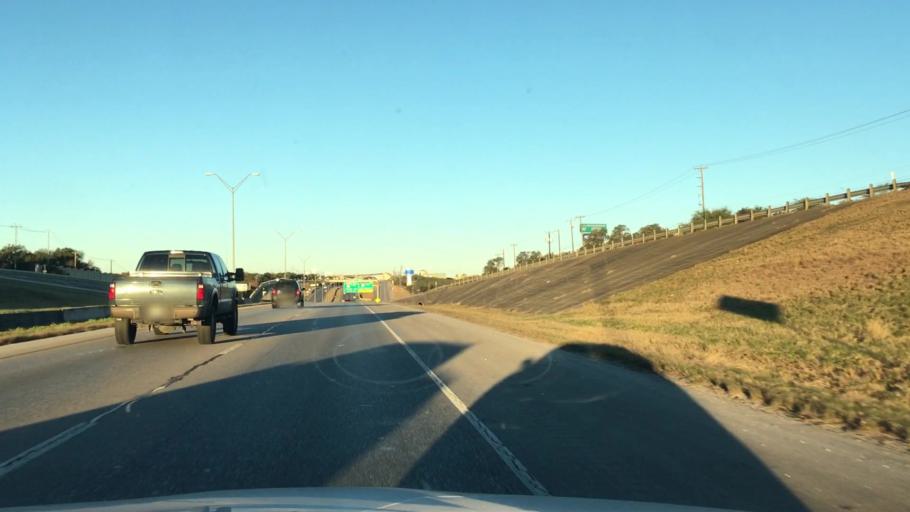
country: US
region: Texas
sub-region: Bexar County
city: Hollywood Park
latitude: 29.5905
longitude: -98.4482
